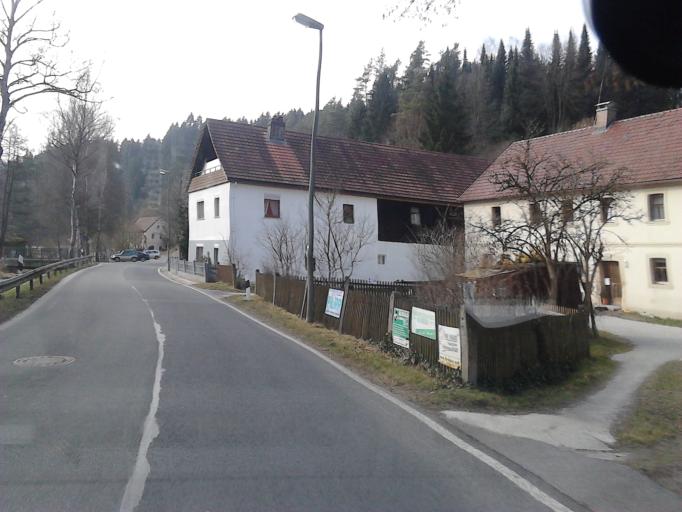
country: DE
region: Bavaria
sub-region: Upper Franconia
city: Hollfeld
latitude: 49.9594
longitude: 11.2377
